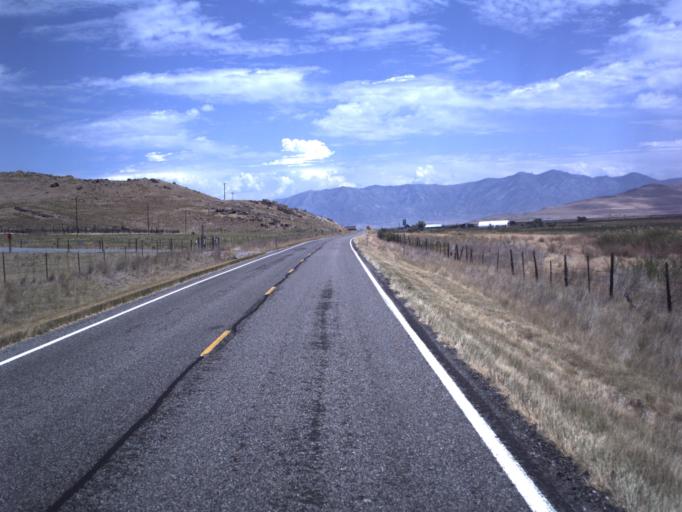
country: US
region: Utah
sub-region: Box Elder County
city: Tremonton
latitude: 41.6213
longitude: -112.3558
